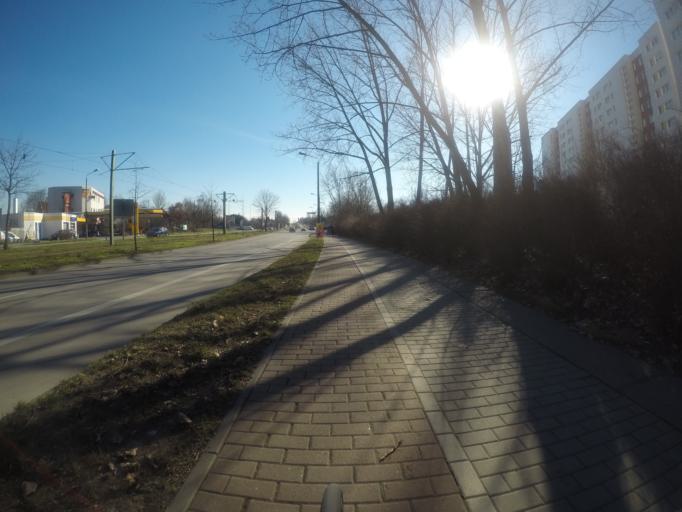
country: DE
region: Berlin
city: Alt-Hohenschoenhausen
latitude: 52.5477
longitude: 13.5084
